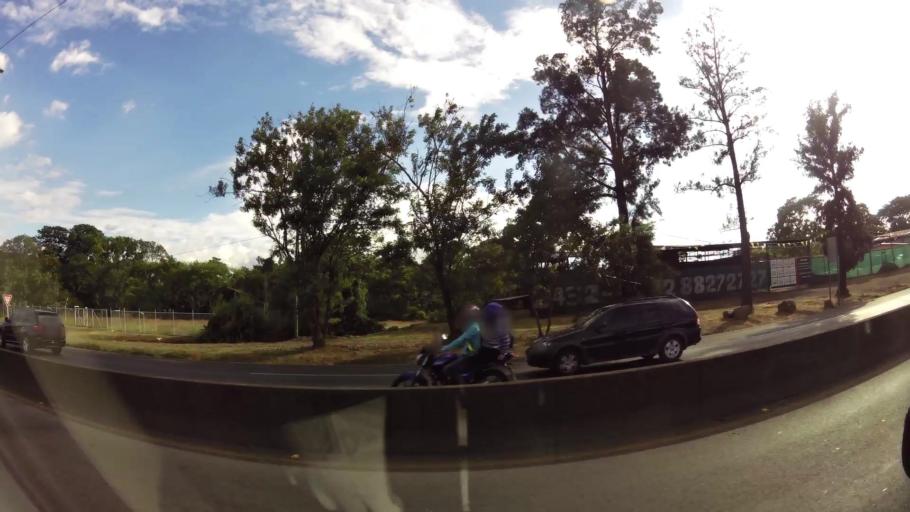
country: CR
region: Heredia
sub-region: Canton de Belen
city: San Antonio
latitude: 10.0026
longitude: -84.1783
